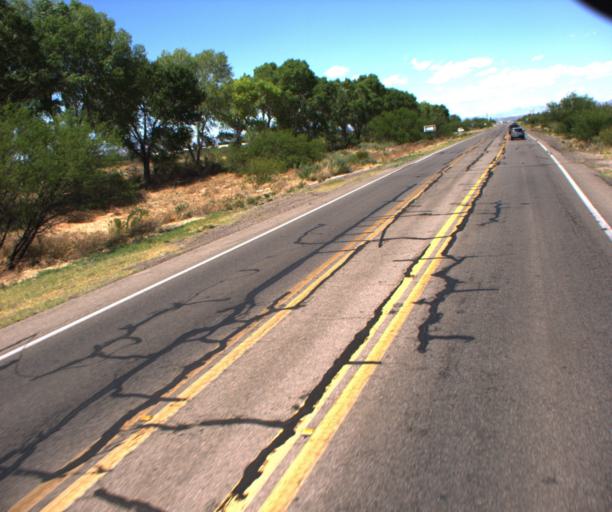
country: US
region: Arizona
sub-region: Cochise County
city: Benson
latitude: 31.9411
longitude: -110.2859
